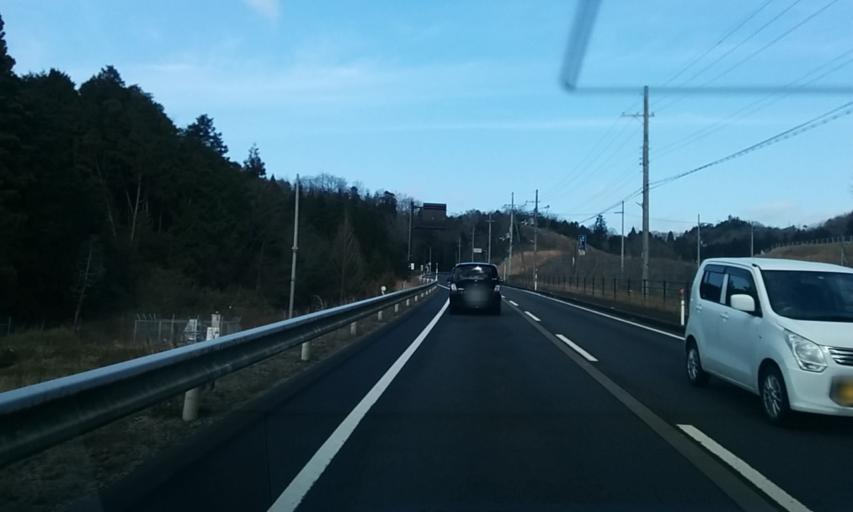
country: JP
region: Kyoto
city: Miyazu
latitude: 35.5787
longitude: 135.1204
